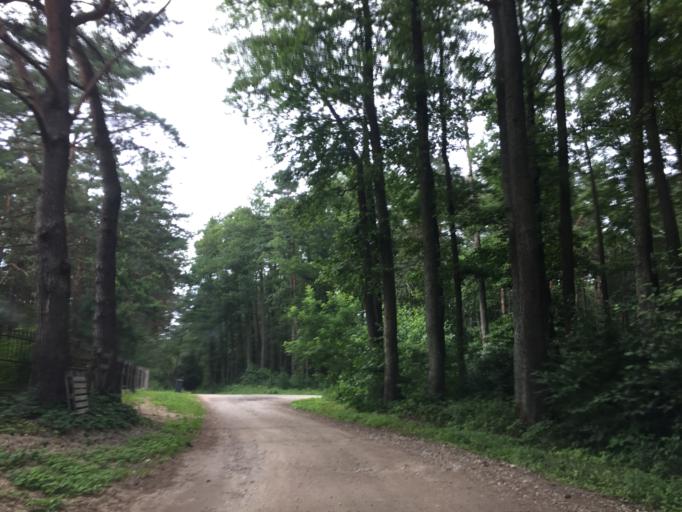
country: LV
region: Riga
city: Jaunciems
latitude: 57.1042
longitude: 24.1932
